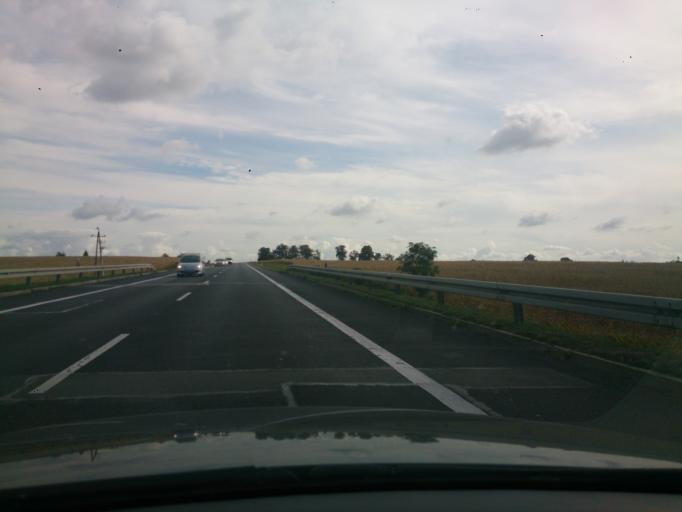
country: PL
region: Kujawsko-Pomorskie
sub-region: Powiat swiecki
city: Swiecie
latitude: 53.4202
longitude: 18.4471
